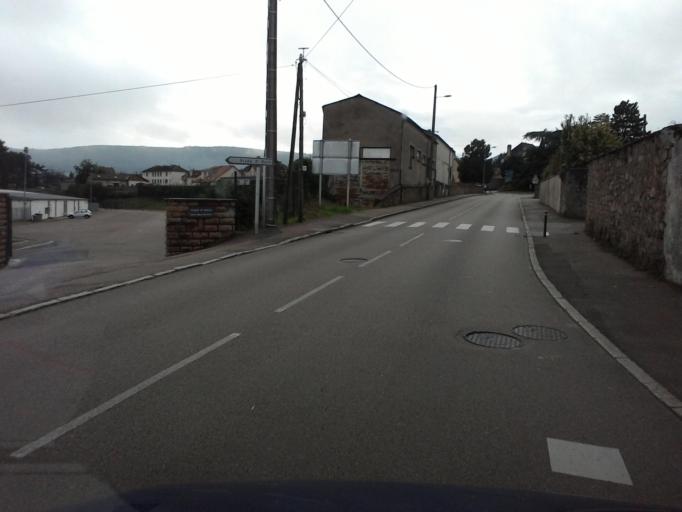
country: FR
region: Bourgogne
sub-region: Departement de Saone-et-Loire
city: Autun
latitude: 46.9571
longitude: 4.3067
